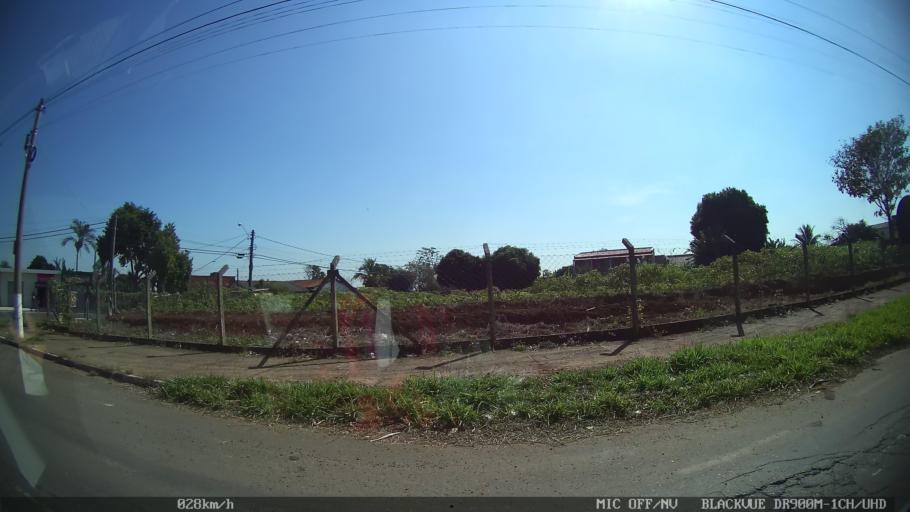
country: BR
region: Sao Paulo
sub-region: Indaiatuba
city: Indaiatuba
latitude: -23.0337
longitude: -47.1049
